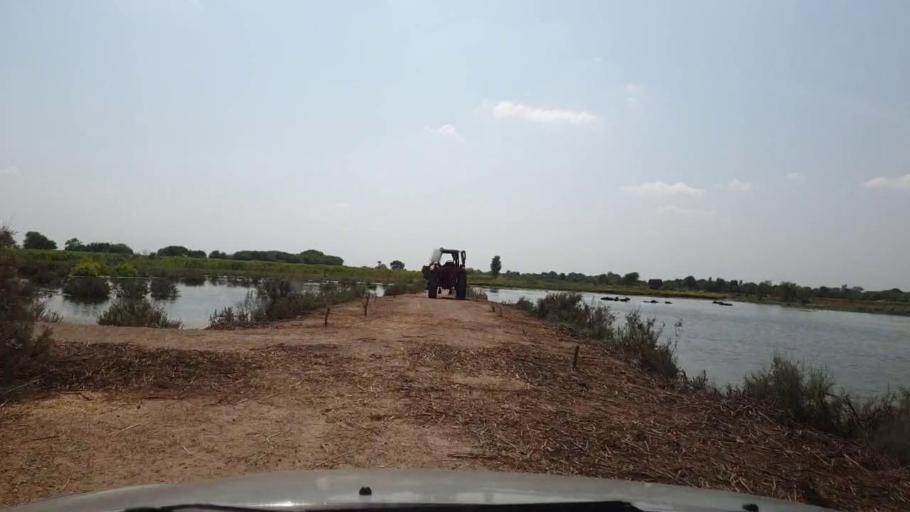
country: PK
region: Sindh
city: Rajo Khanani
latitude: 24.9979
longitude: 68.7686
